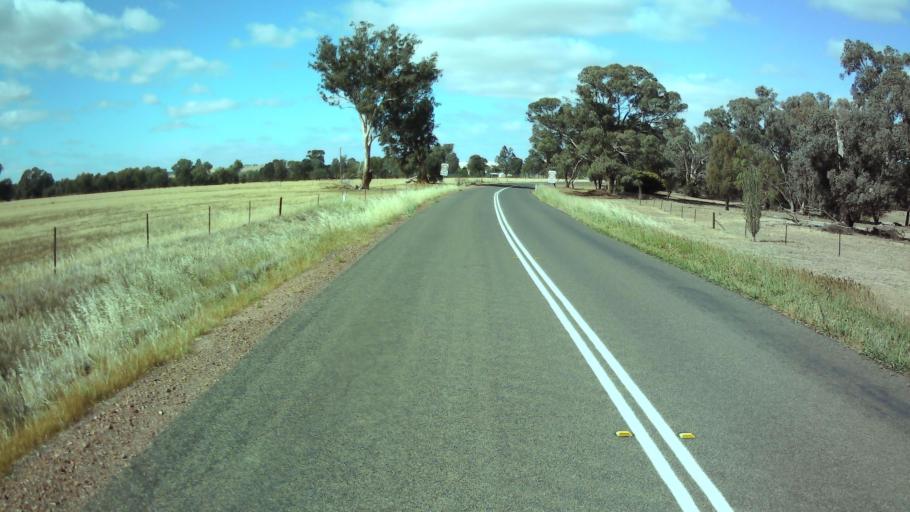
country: AU
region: New South Wales
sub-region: Weddin
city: Grenfell
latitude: -33.9911
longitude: 148.4085
